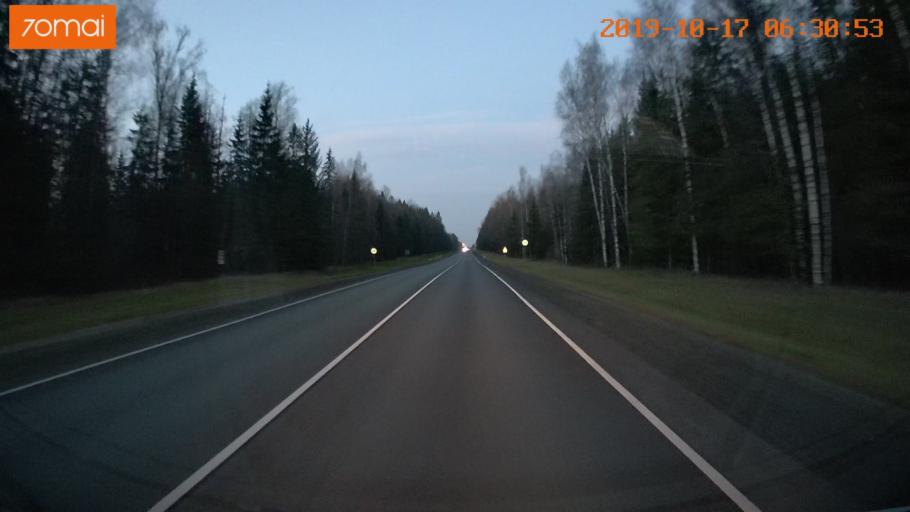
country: RU
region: Ivanovo
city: Lezhnevo
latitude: 56.7324
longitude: 40.7100
